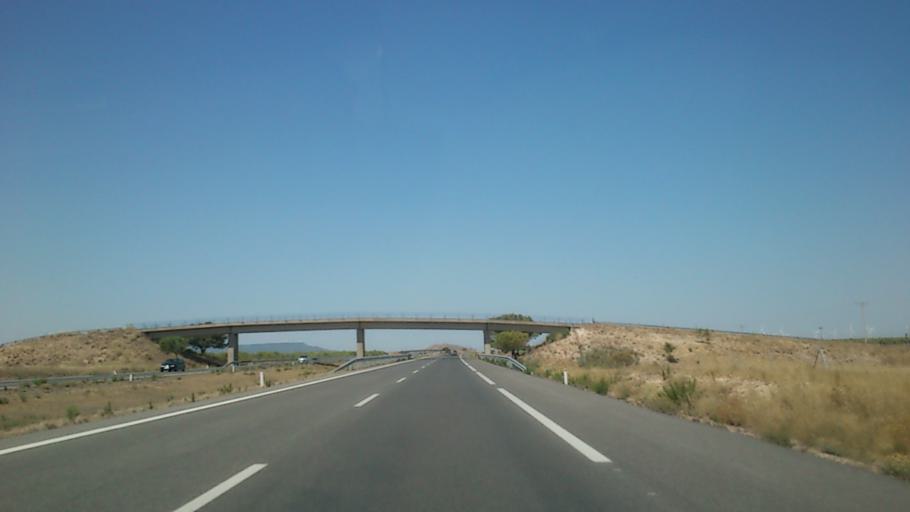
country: ES
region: Aragon
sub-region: Provincia de Zaragoza
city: Gallur
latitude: 41.8392
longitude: -1.3396
